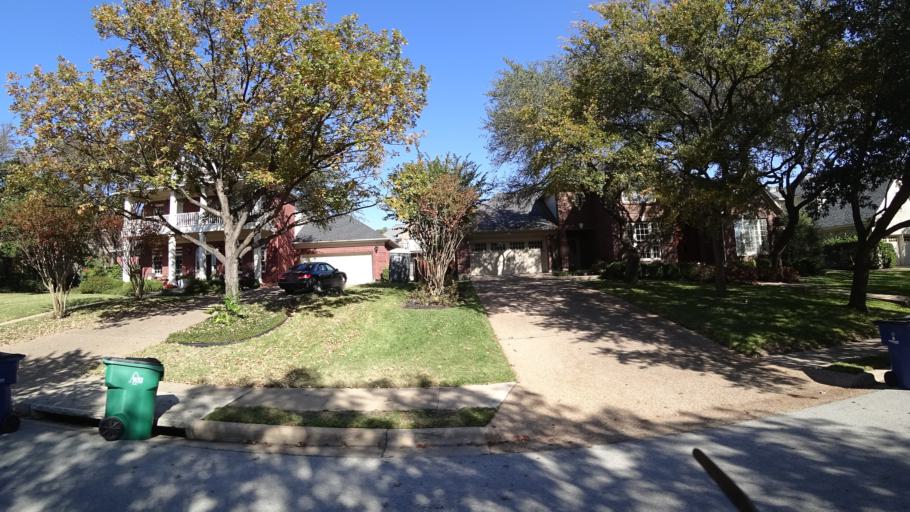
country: US
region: Texas
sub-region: Travis County
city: Lost Creek
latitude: 30.3742
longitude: -97.8505
